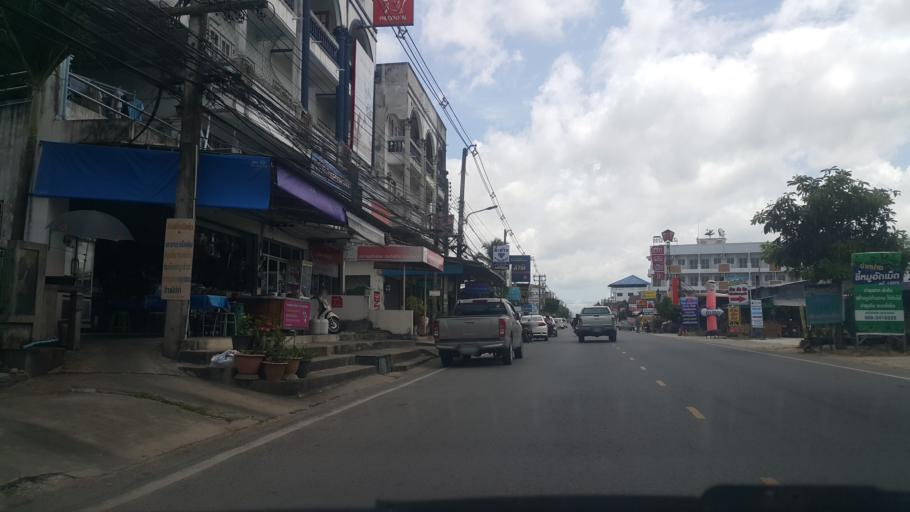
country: TH
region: Rayong
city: Ban Chang
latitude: 12.7288
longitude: 101.0517
